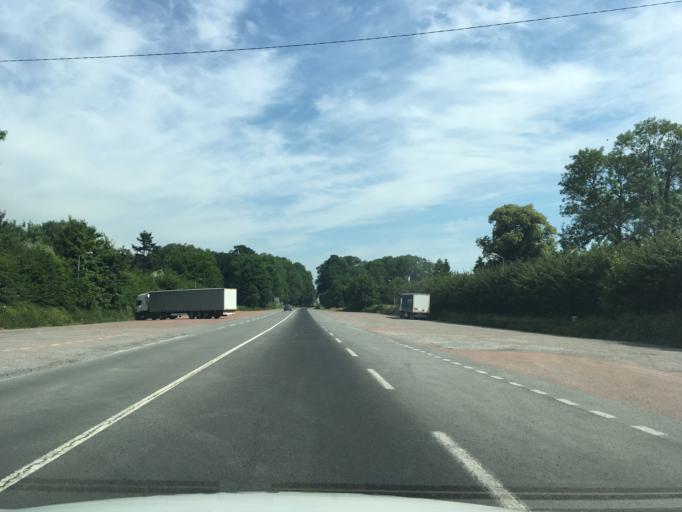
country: FR
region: Picardie
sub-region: Departement de la Somme
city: Chaulnes
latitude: 49.8103
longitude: 2.8468
